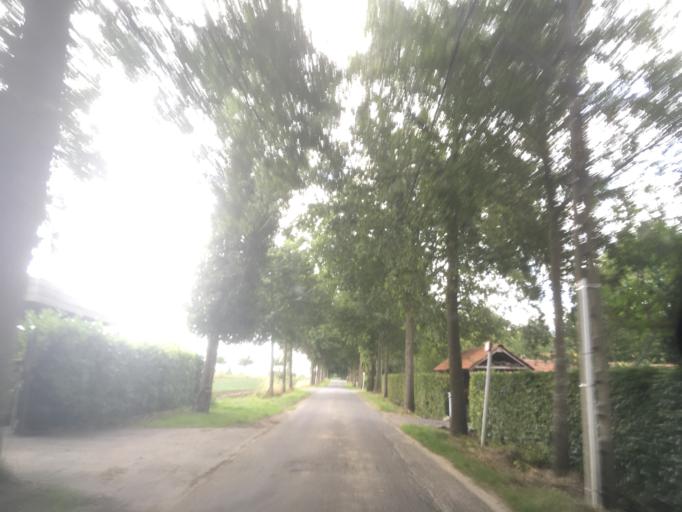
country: BE
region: Flanders
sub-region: Provincie West-Vlaanderen
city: Moorslede
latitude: 50.9032
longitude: 3.0983
